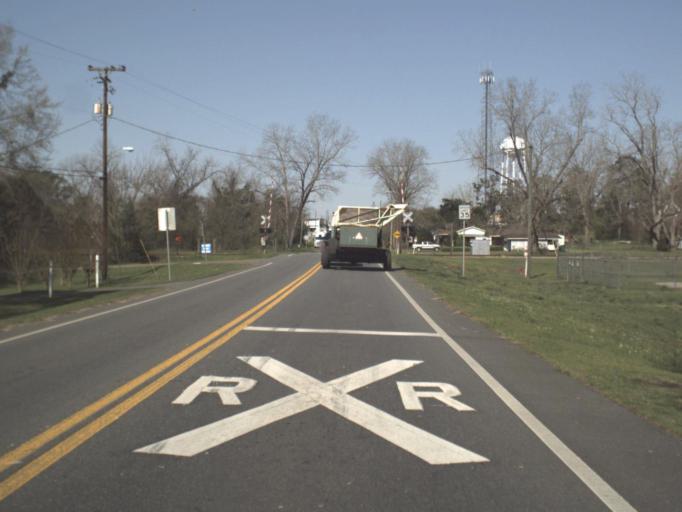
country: US
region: Florida
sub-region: Jackson County
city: Graceville
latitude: 30.9496
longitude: -85.3977
